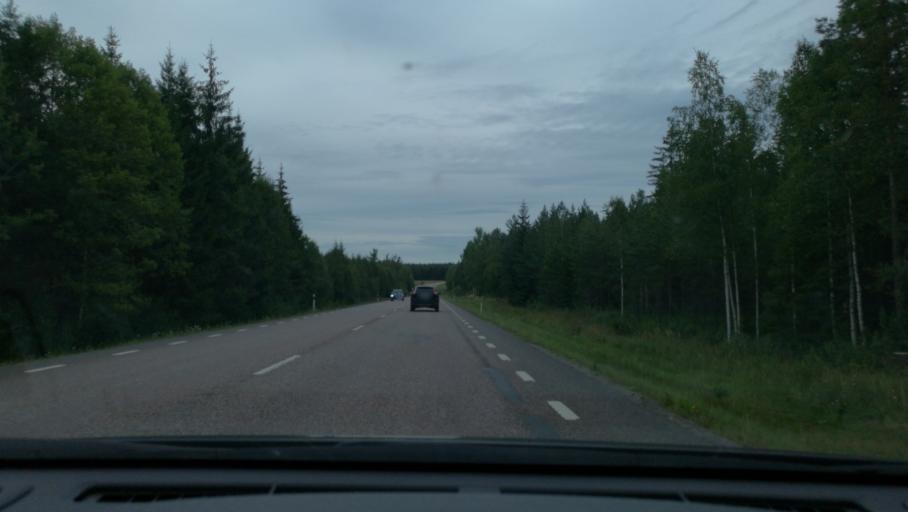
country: SE
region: Soedermanland
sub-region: Katrineholms Kommun
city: Katrineholm
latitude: 59.0495
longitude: 16.2211
